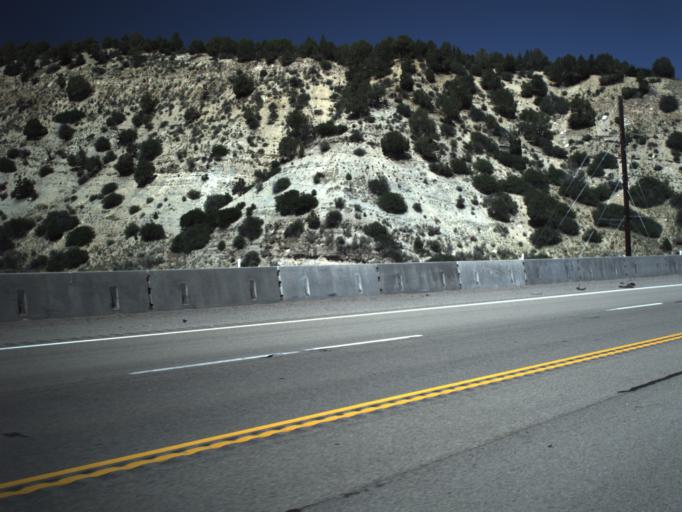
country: US
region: Utah
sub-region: Sanpete County
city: Fairview
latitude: 39.9319
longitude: -111.1996
